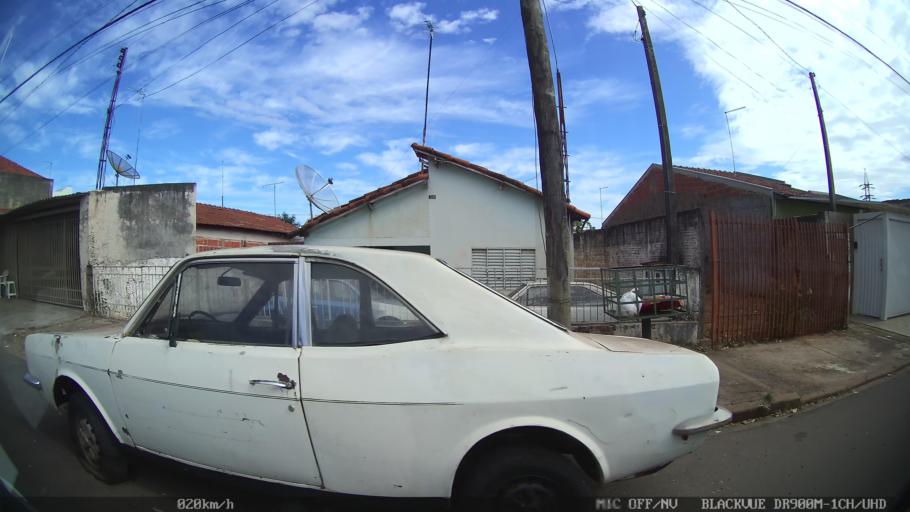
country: BR
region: Sao Paulo
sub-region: Bady Bassitt
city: Bady Bassitt
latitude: -20.8151
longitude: -49.5231
